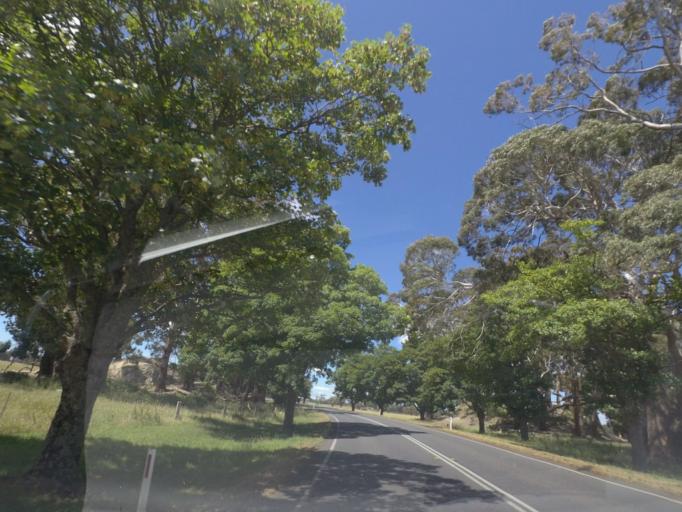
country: AU
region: Victoria
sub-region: Mount Alexander
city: Castlemaine
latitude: -37.3351
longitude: 144.1677
